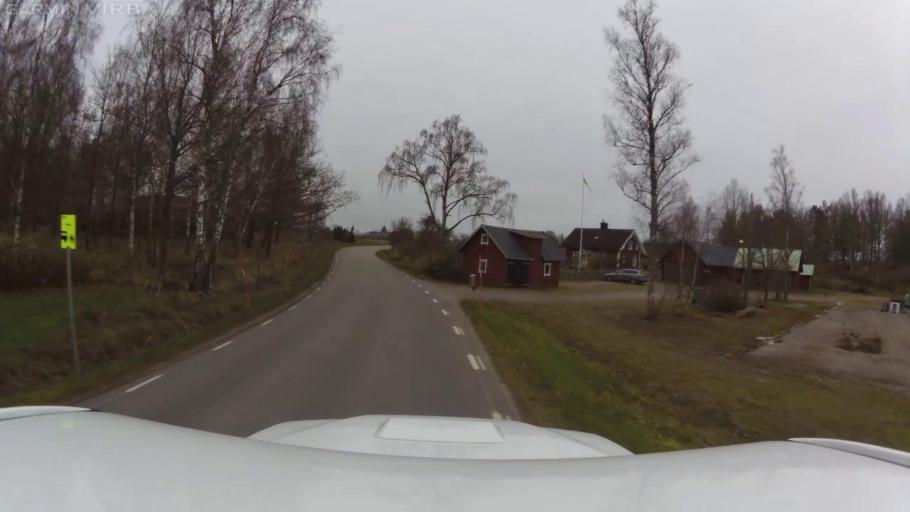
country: SE
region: OEstergoetland
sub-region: Linkopings Kommun
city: Vikingstad
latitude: 58.3140
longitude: 15.3753
